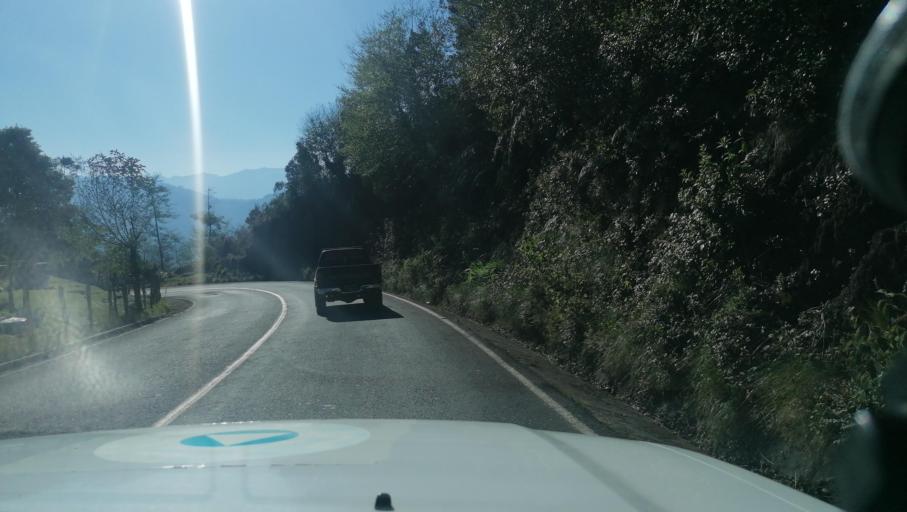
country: MX
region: Chiapas
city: Motozintla de Mendoza
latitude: 15.2437
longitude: -92.2299
